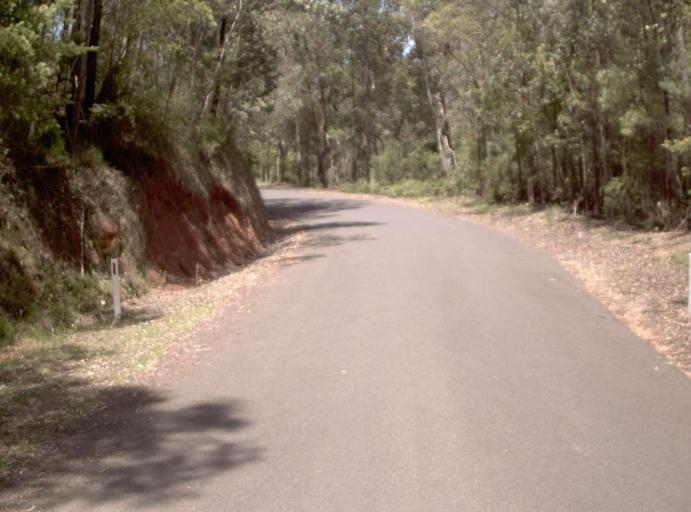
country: AU
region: New South Wales
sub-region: Bombala
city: Bombala
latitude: -37.4428
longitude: 148.9634
